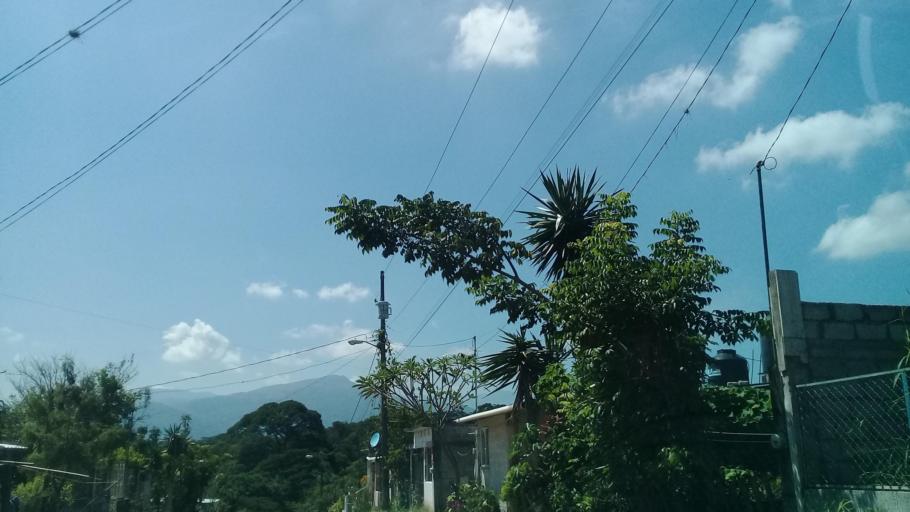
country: MX
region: Veracruz
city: Amatlan de los Reyes
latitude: 18.8380
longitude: -96.9150
